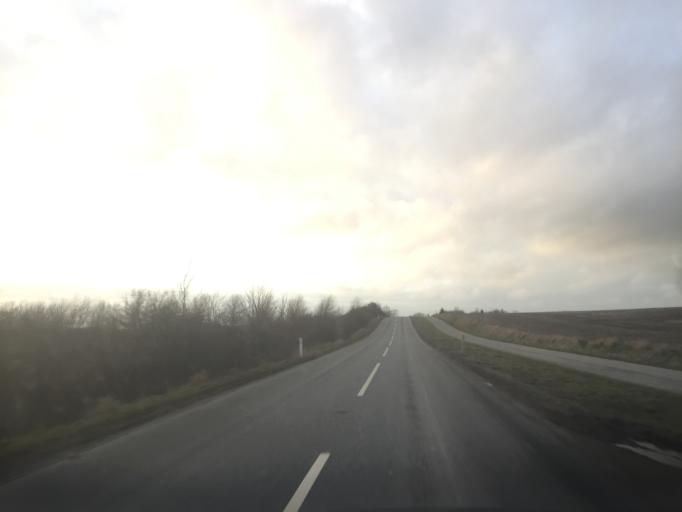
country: DK
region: Capital Region
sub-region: Egedal Kommune
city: Smorumnedre
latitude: 55.7072
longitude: 12.3188
